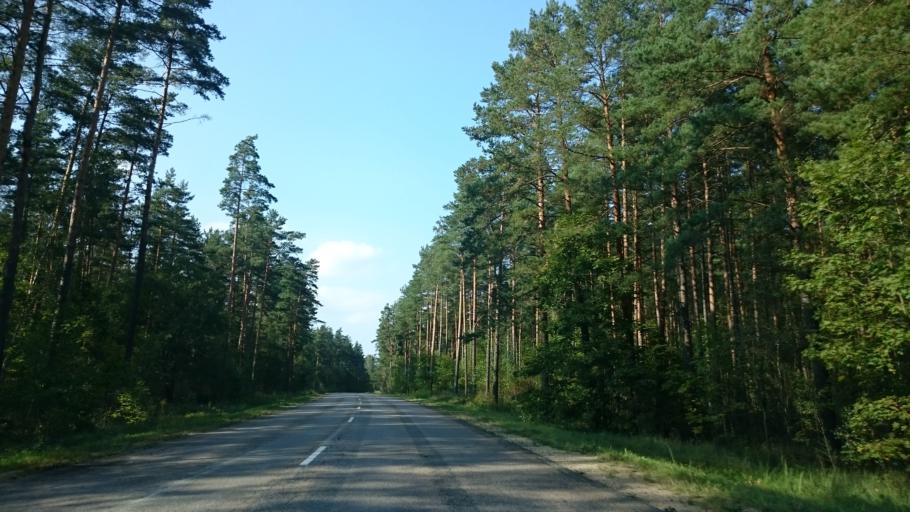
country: LV
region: Stopini
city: Ulbroka
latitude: 56.9574
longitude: 24.3083
